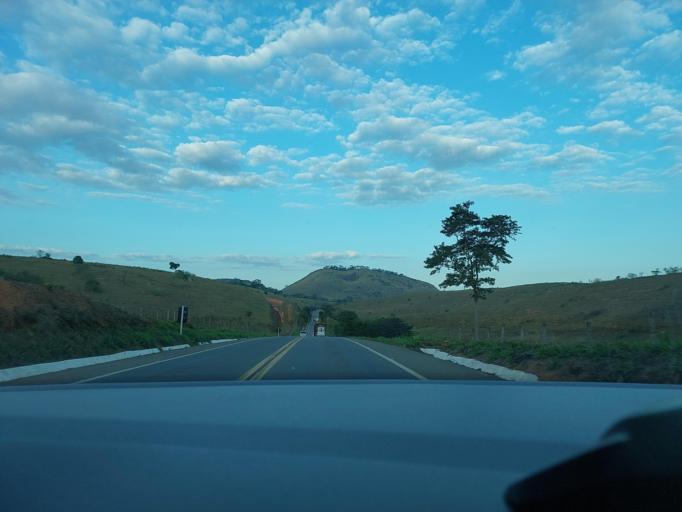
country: BR
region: Rio de Janeiro
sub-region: Natividade
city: Natividade
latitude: -21.1542
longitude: -42.1379
